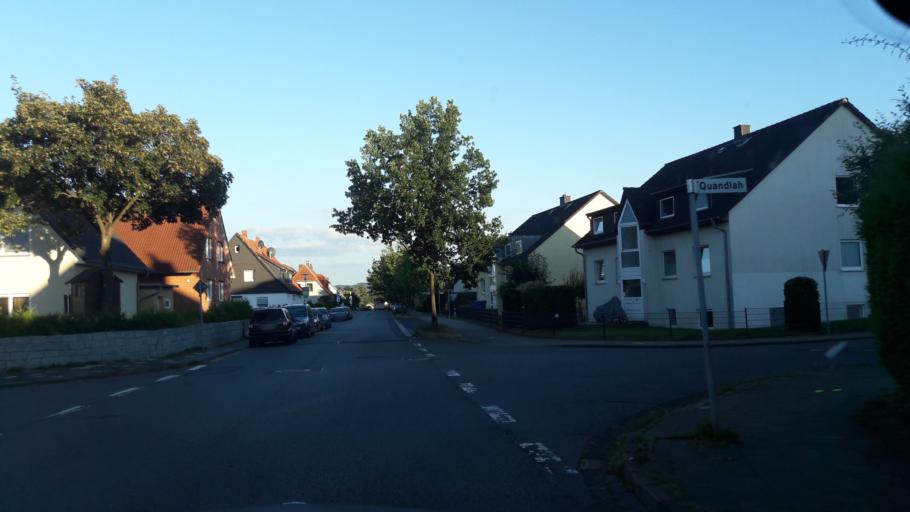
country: DE
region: Lower Saxony
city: Hildesheim
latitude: 52.1187
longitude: 9.9918
